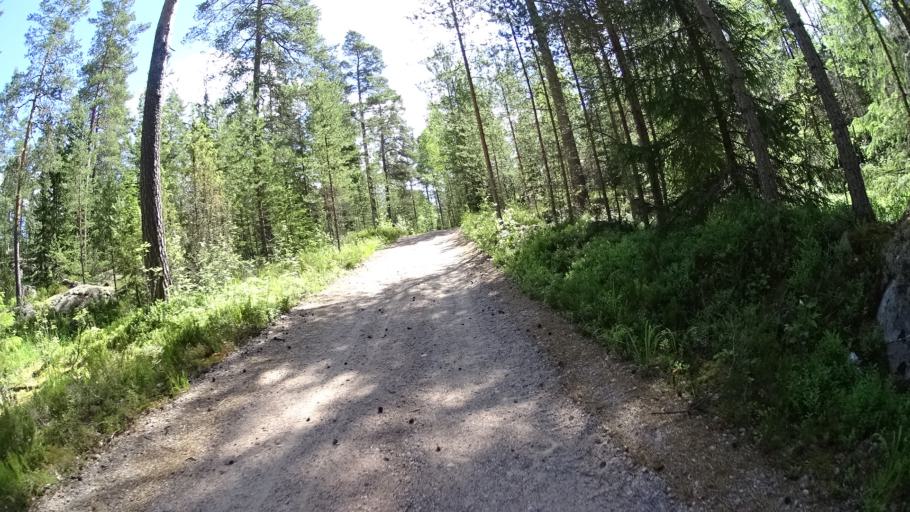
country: FI
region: Uusimaa
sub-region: Helsinki
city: Vihti
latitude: 60.3294
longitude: 24.4756
